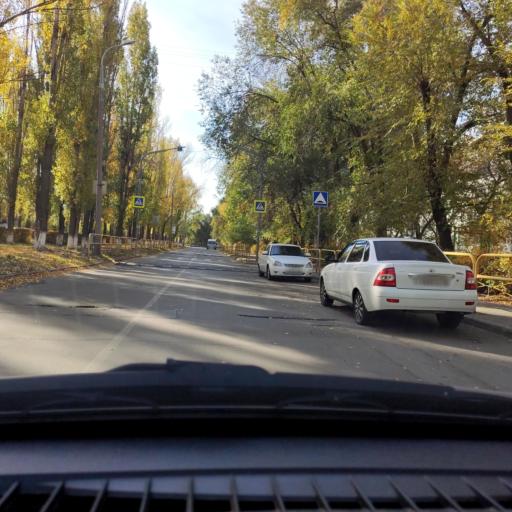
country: RU
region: Samara
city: Tol'yatti
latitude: 53.5230
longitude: 49.2698
